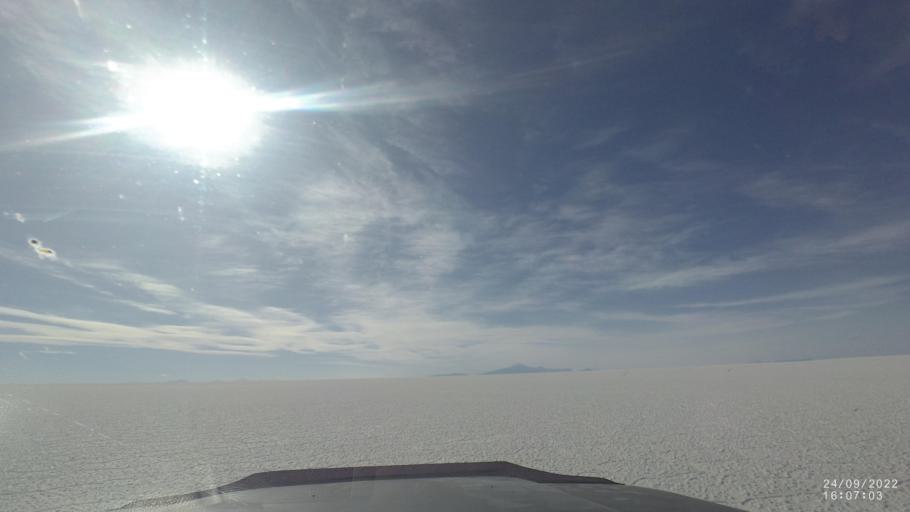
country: BO
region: Potosi
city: Colchani
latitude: -20.3022
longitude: -67.2993
